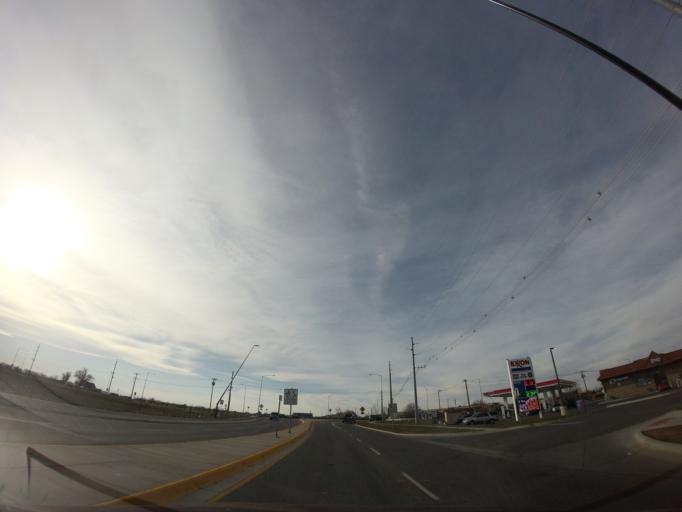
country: US
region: Montana
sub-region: Yellowstone County
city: Billings
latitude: 45.7842
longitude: -108.6169
